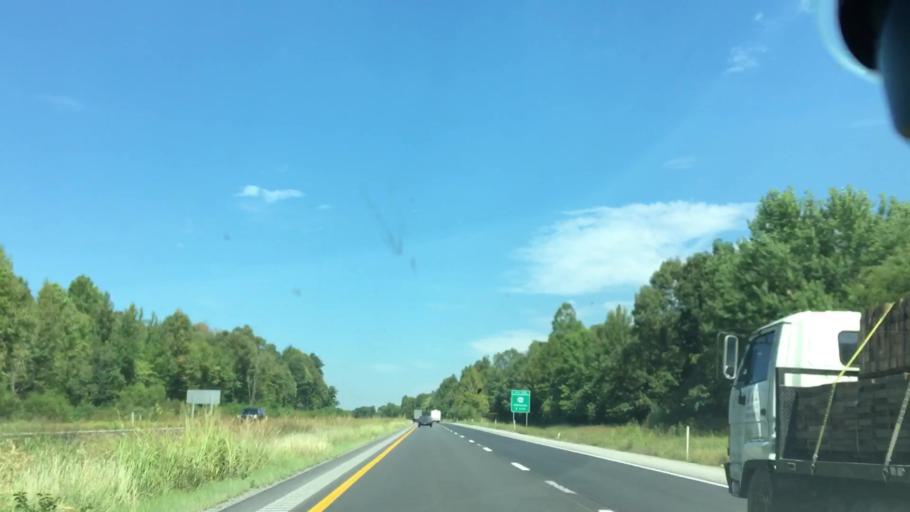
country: US
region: Kentucky
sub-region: Hopkins County
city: Madisonville
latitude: 37.3825
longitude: -87.4810
